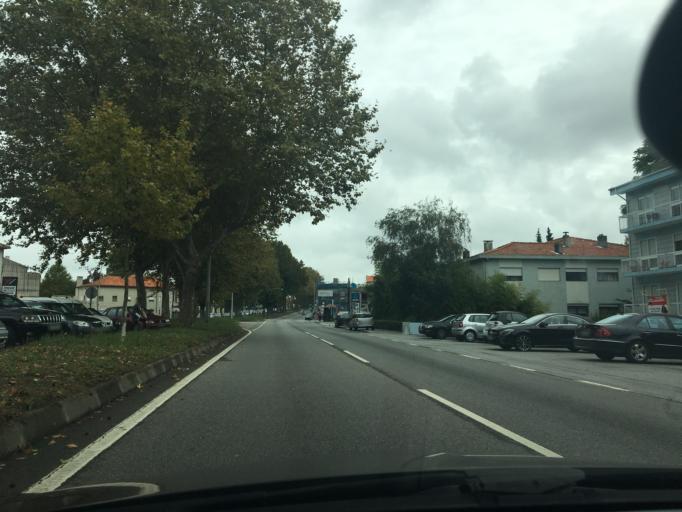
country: PT
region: Porto
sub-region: Matosinhos
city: Senhora da Hora
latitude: 41.1819
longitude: -8.6475
